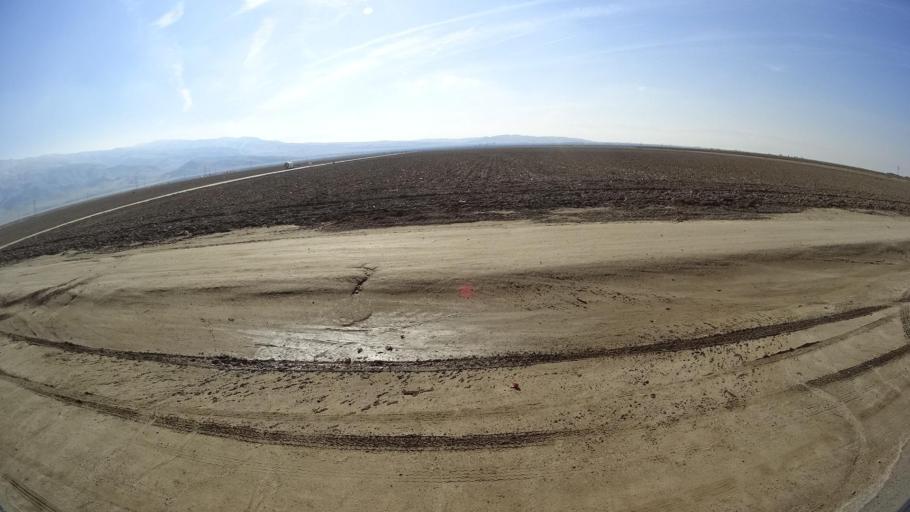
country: US
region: California
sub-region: Kern County
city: Arvin
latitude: 35.1946
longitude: -118.8113
